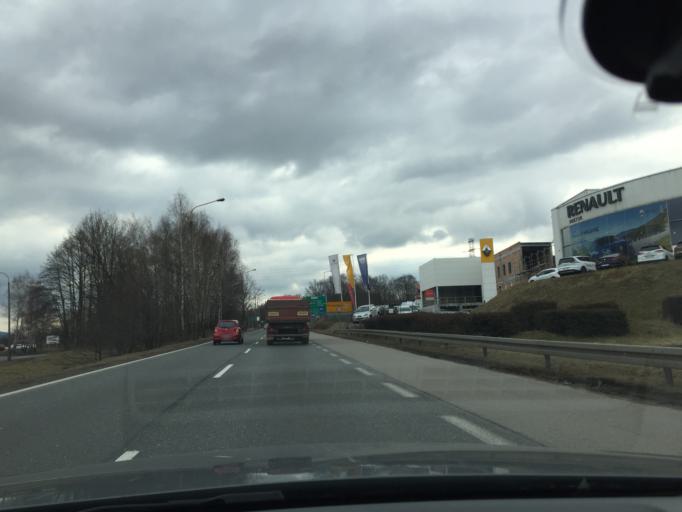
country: PL
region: Silesian Voivodeship
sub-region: Bielsko-Biala
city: Bielsko-Biala
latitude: 49.8544
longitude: 19.0275
